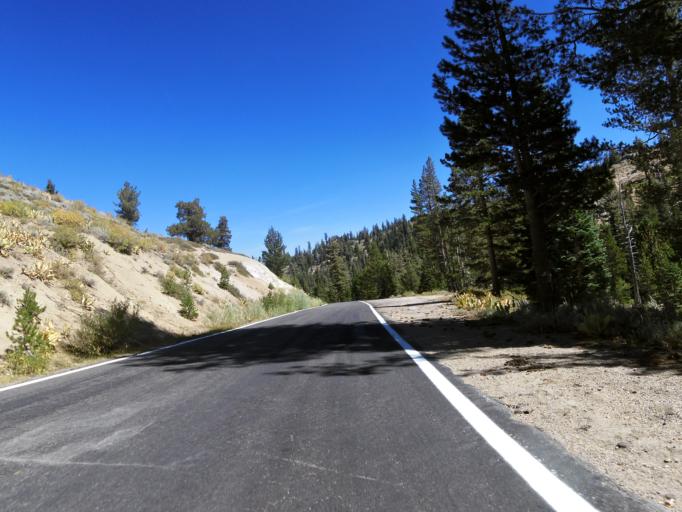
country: US
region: Nevada
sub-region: Douglas County
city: Gardnerville Ranchos
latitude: 38.5621
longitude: -119.8067
